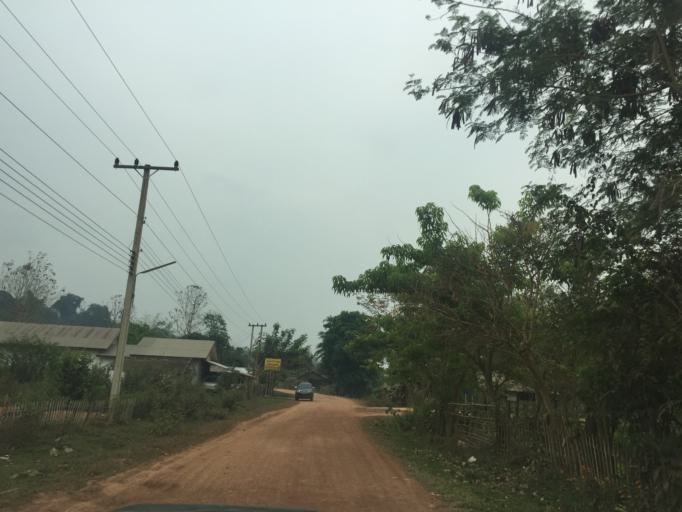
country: TH
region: Loei
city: Pak Chom
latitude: 18.5465
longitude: 101.6029
